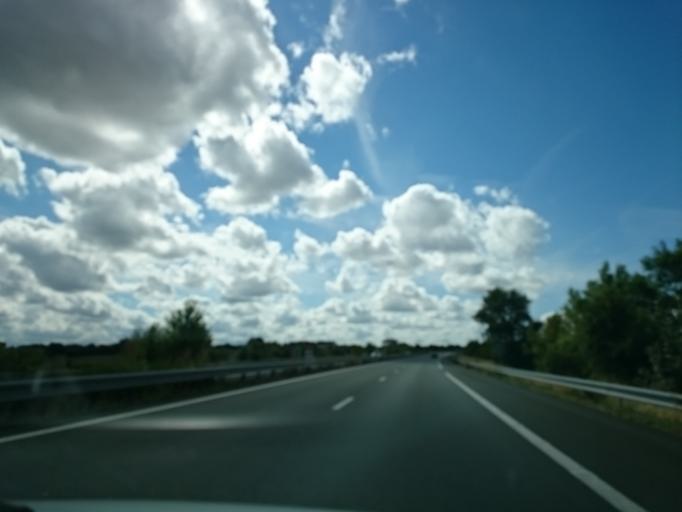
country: FR
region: Pays de la Loire
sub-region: Departement de Maine-et-Loire
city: Ingrandes
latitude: 47.4222
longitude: -0.9460
